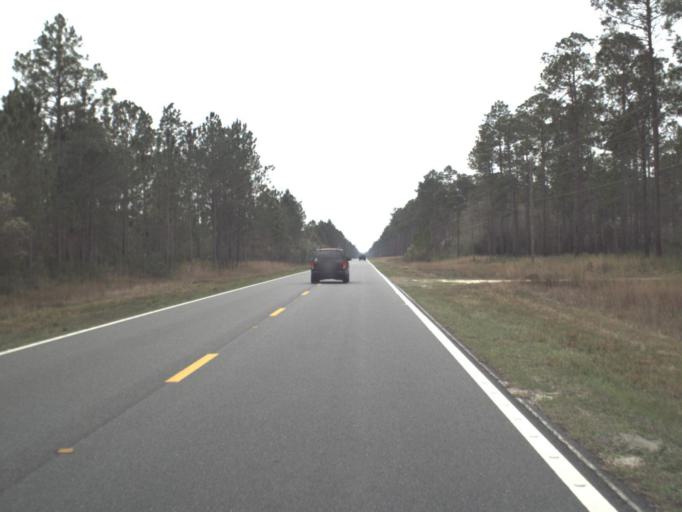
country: US
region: Florida
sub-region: Liberty County
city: Bristol
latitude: 30.2446
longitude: -84.8677
